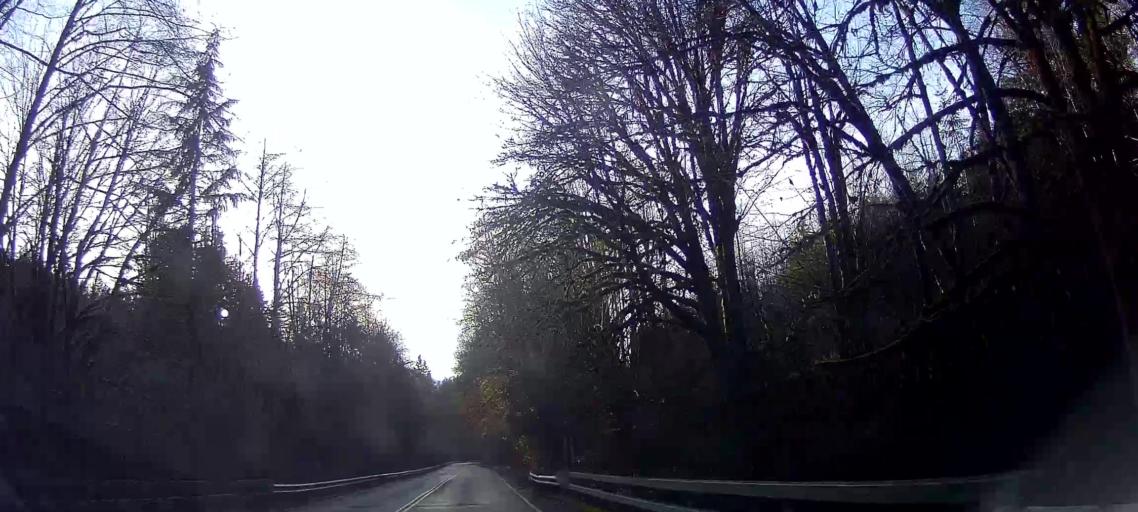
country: US
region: Washington
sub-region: Skagit County
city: Sedro-Woolley
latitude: 48.5517
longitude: -121.8634
